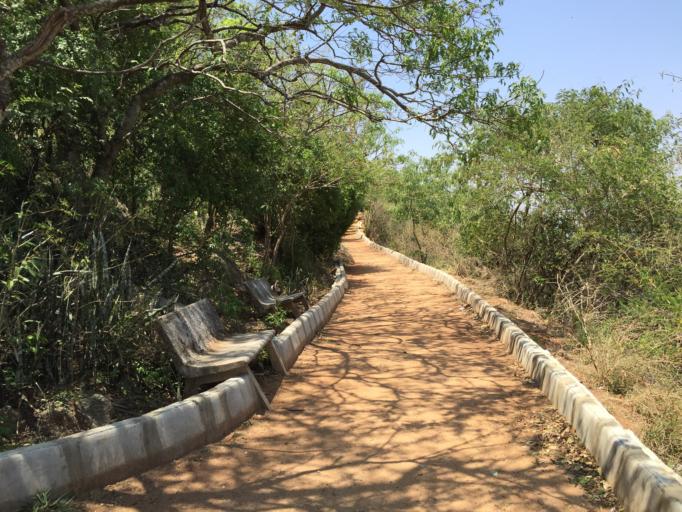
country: IN
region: Karnataka
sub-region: Chikkaballapur
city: Chik Ballapur
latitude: 13.3694
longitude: 77.6862
